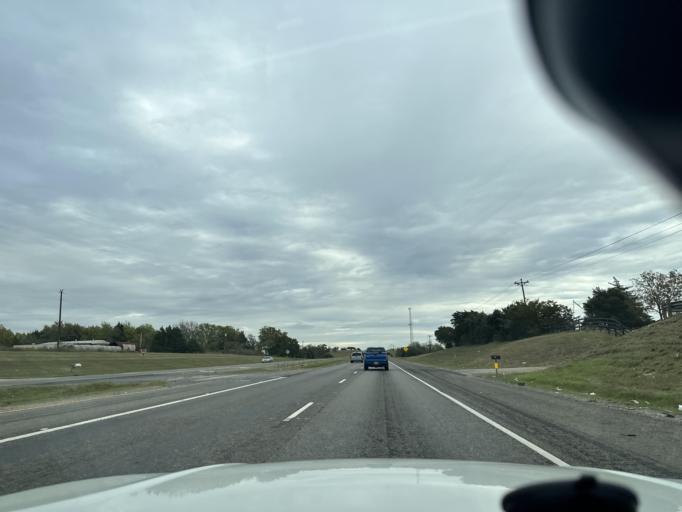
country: US
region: Texas
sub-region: Washington County
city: Brenham
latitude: 30.1907
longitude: -96.5280
